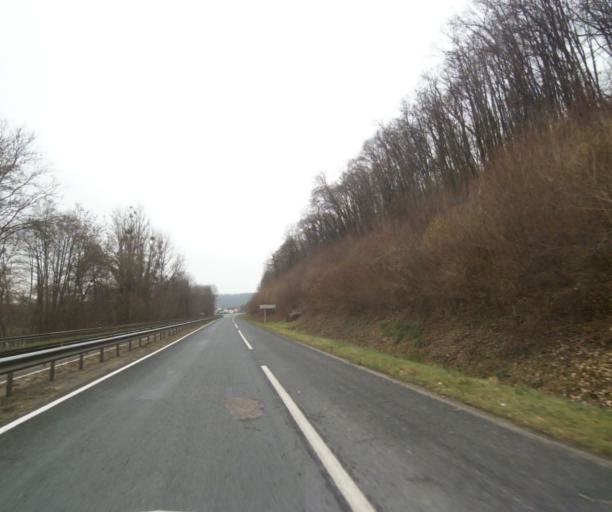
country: FR
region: Champagne-Ardenne
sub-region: Departement de la Haute-Marne
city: Chevillon
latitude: 48.5359
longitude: 5.0980
